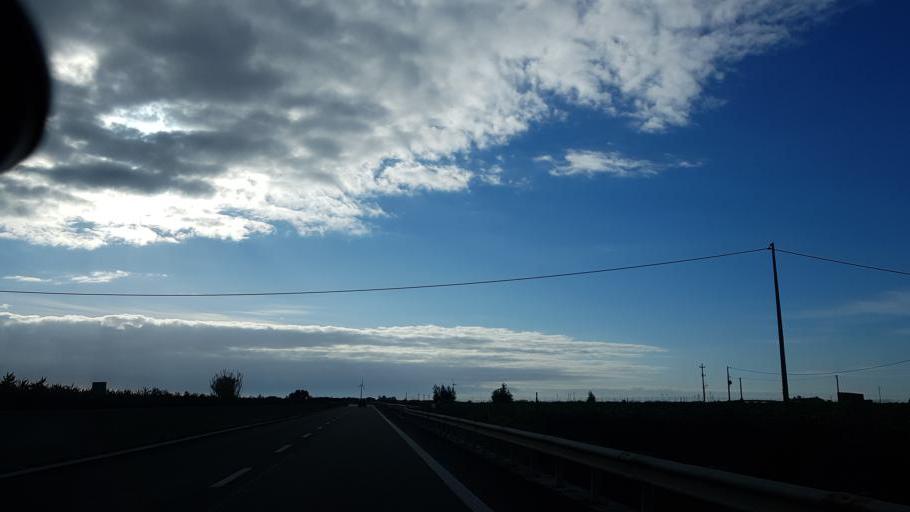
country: IT
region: Apulia
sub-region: Provincia di Brindisi
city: La Rosa
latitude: 40.5879
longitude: 17.9739
